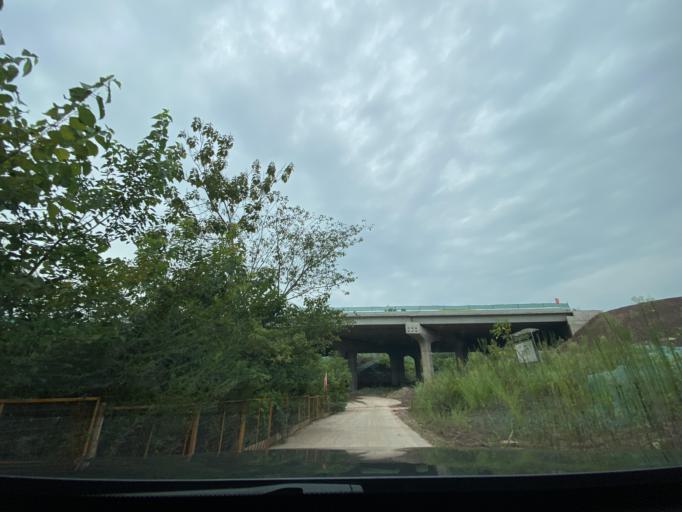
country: CN
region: Sichuan
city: Jiancheng
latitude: 30.3877
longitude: 104.5017
